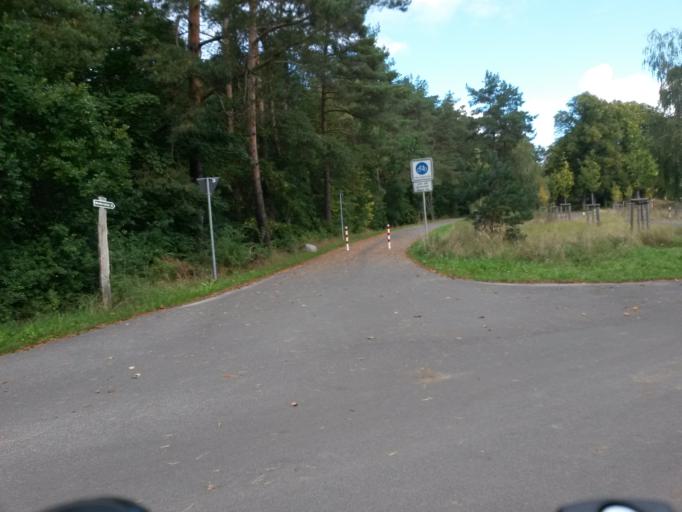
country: DE
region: Brandenburg
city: Templin
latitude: 53.1803
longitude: 13.5132
